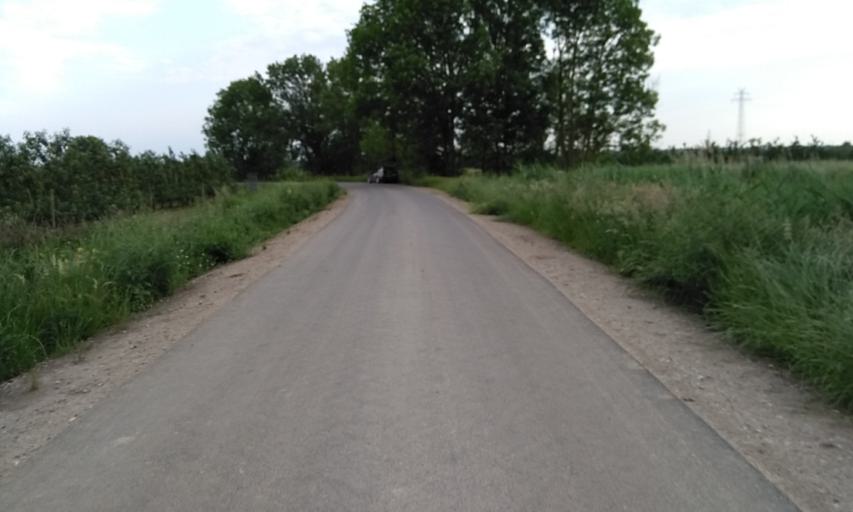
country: DE
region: Lower Saxony
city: Mittelnkirchen
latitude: 53.5205
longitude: 9.6371
